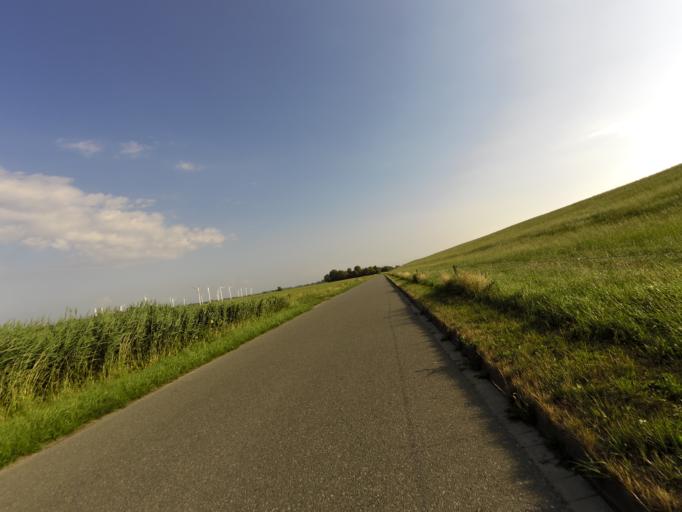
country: DE
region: Lower Saxony
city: Nordholz
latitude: 53.8075
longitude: 8.5708
